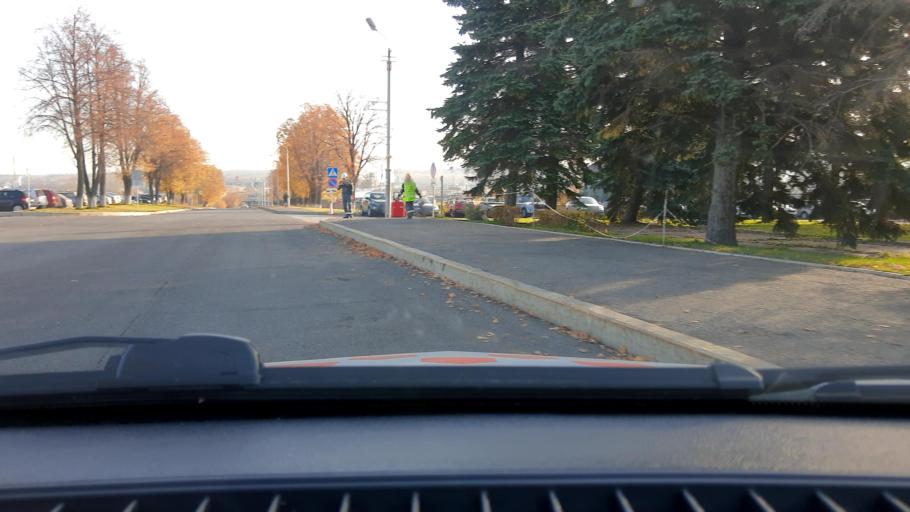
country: RU
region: Bashkortostan
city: Ufa
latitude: 54.8739
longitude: 56.0918
